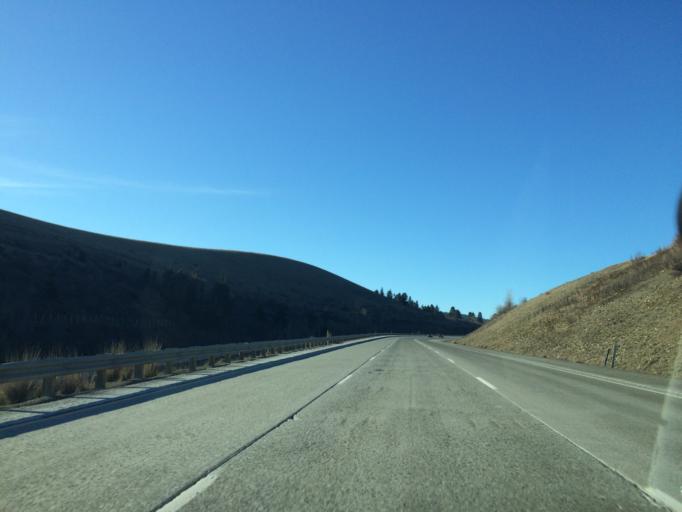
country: US
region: Washington
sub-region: Kittitas County
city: Cle Elum
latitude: 47.0923
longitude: -120.7494
